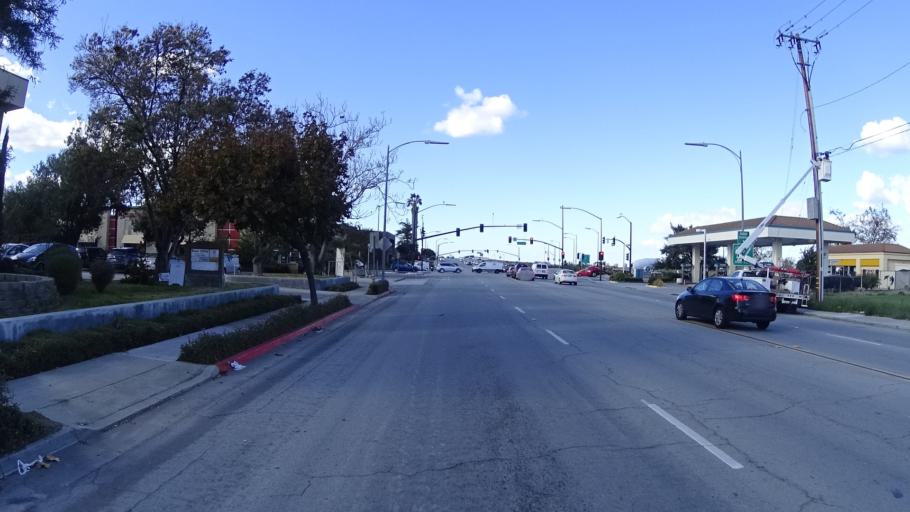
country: US
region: California
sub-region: Santa Clara County
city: San Jose
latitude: 37.3456
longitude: -121.9145
